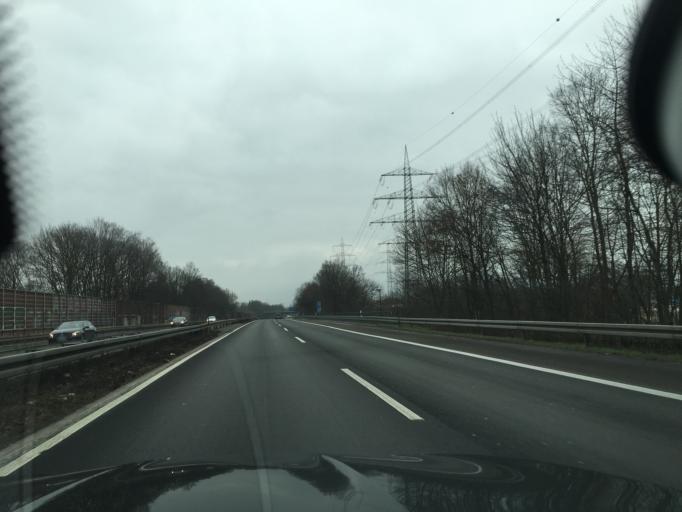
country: DE
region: North Rhine-Westphalia
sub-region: Regierungsbezirk Koln
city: Troisdorf
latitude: 50.8135
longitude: 7.1220
